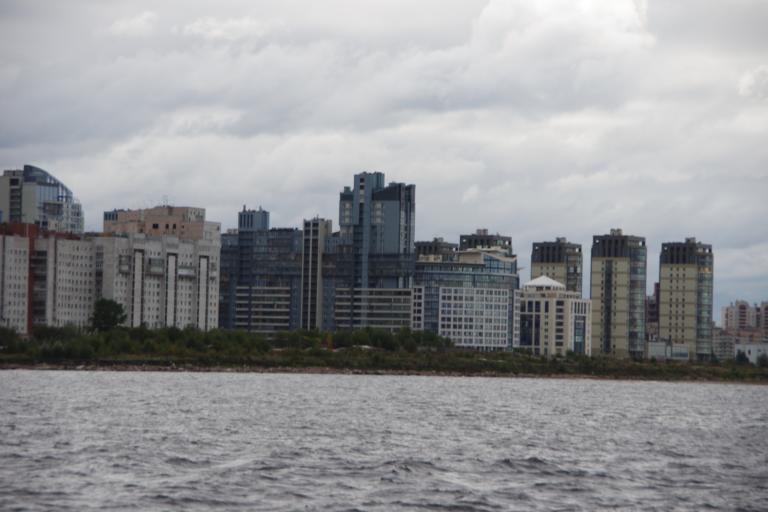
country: RU
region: St.-Petersburg
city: Staraya Derevnya
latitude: 59.9670
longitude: 30.2090
